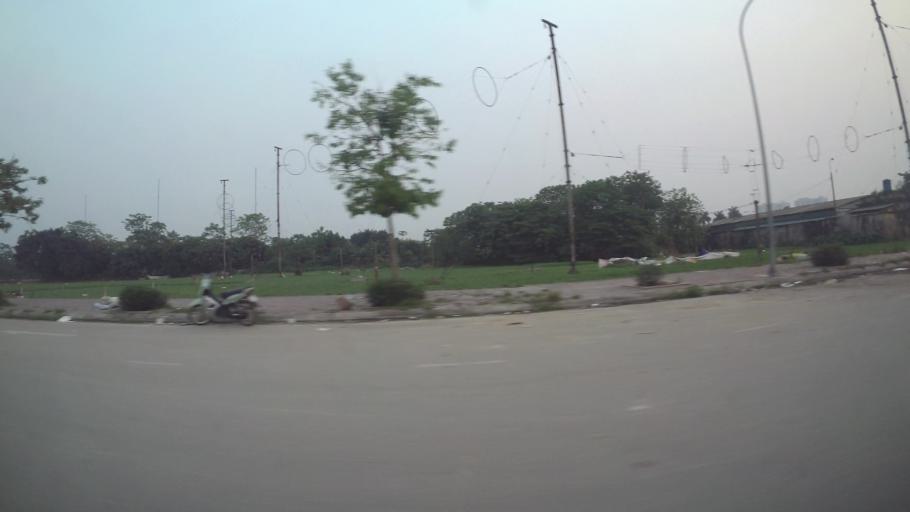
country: VN
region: Ha Noi
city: Thanh Xuan
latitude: 20.9771
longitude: 105.7993
